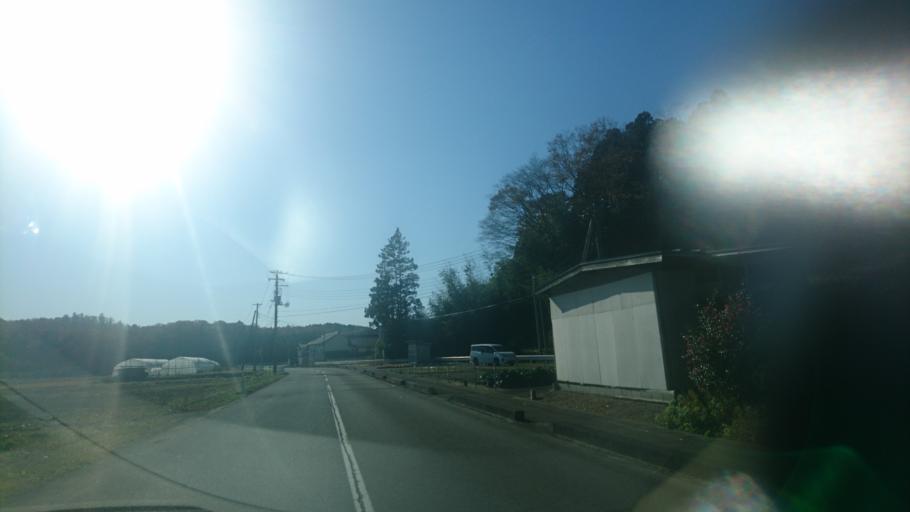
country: JP
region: Miyagi
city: Tomiya
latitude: 38.4097
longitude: 140.8723
